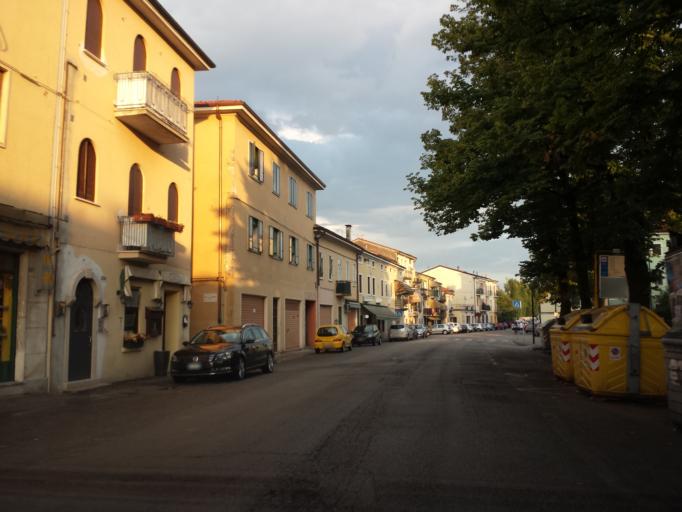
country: IT
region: Veneto
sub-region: Provincia di Vicenza
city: Villaggio Montegrappa
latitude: 45.5397
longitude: 11.5830
